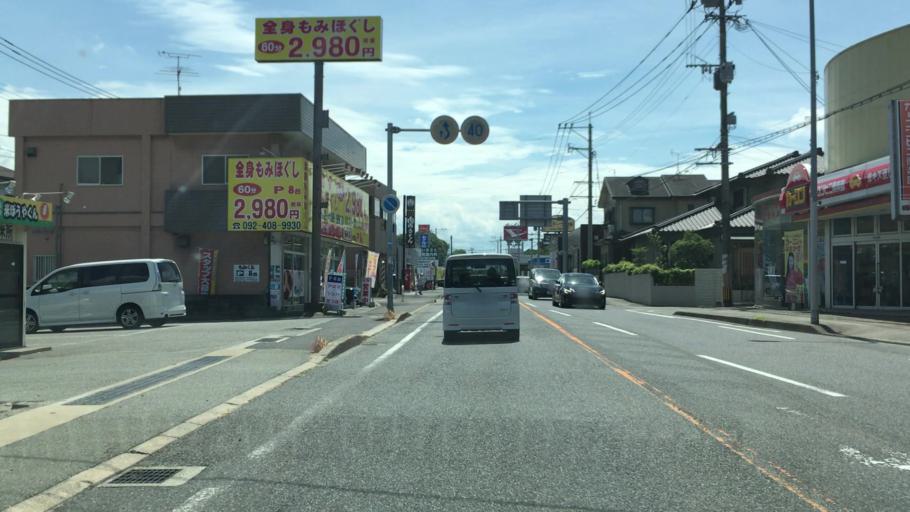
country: JP
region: Fukuoka
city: Onojo
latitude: 33.5242
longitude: 130.4960
